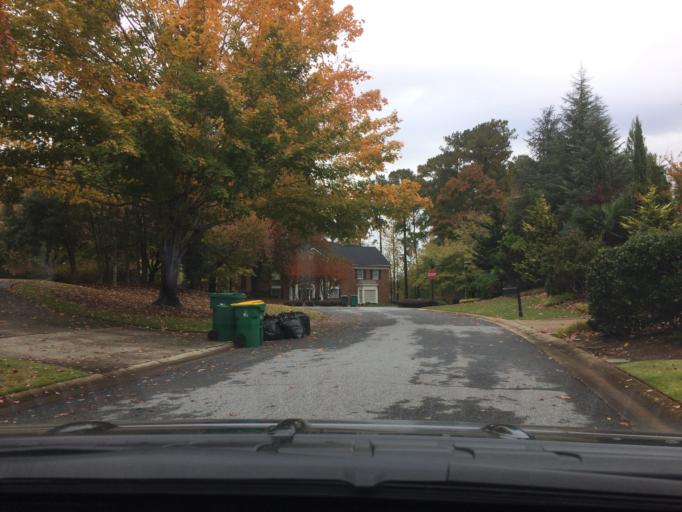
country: US
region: Georgia
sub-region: Fulton County
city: Johns Creek
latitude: 34.0084
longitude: -84.2354
